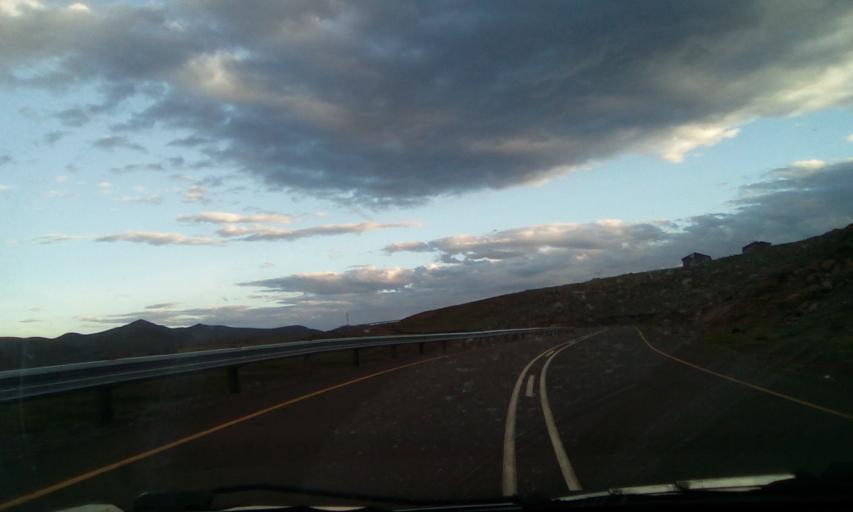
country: LS
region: Maseru
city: Nako
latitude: -29.8152
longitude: 28.0343
